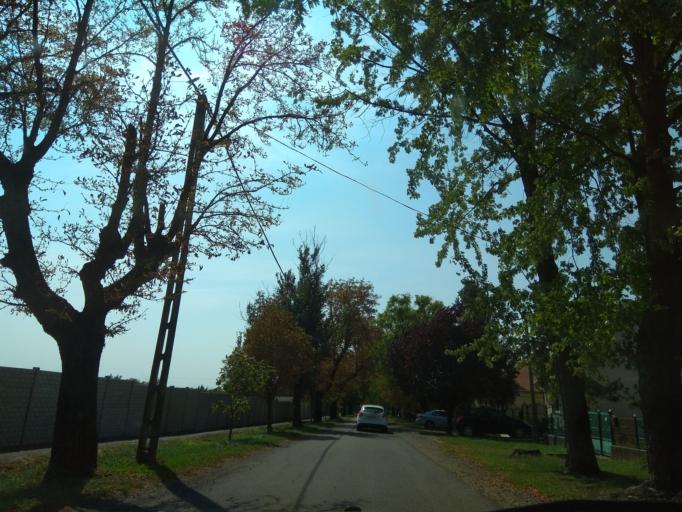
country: HU
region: Borsod-Abauj-Zemplen
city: Tallya
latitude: 48.2318
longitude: 21.2276
